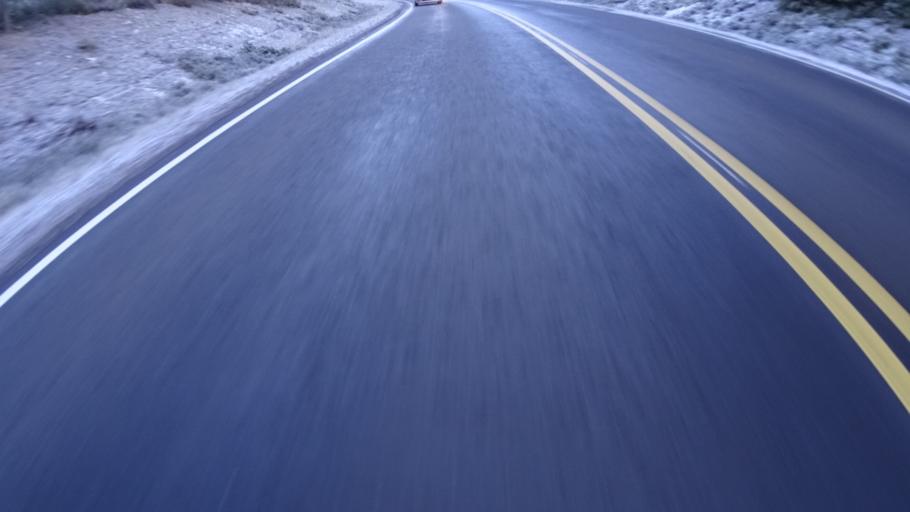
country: FI
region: Uusimaa
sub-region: Helsinki
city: Vihti
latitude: 60.5123
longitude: 24.4385
